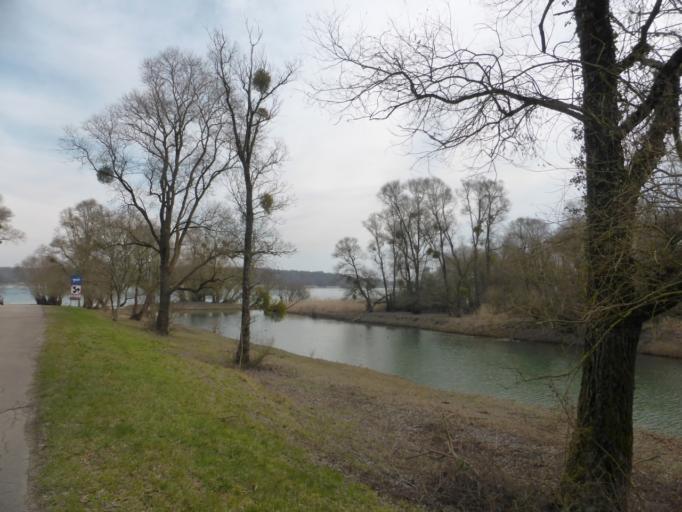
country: FR
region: Champagne-Ardenne
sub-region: Departement de l'Aube
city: Lusigny-sur-Barse
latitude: 48.2836
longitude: 4.3102
